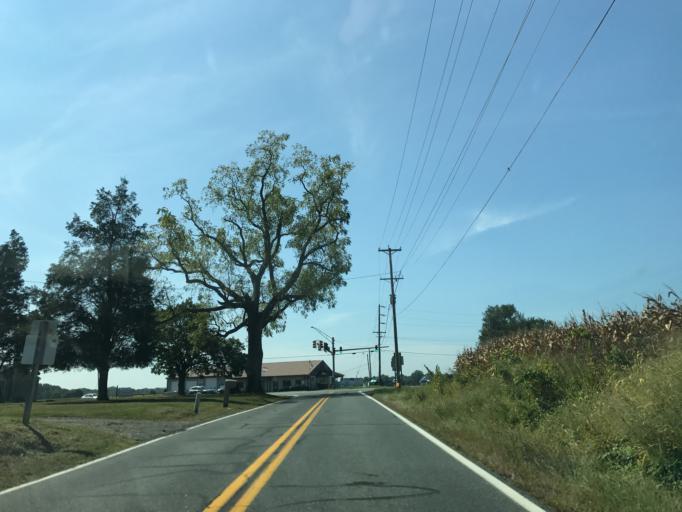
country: US
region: Maryland
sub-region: Cecil County
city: Elkton
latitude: 39.4866
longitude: -75.8471
